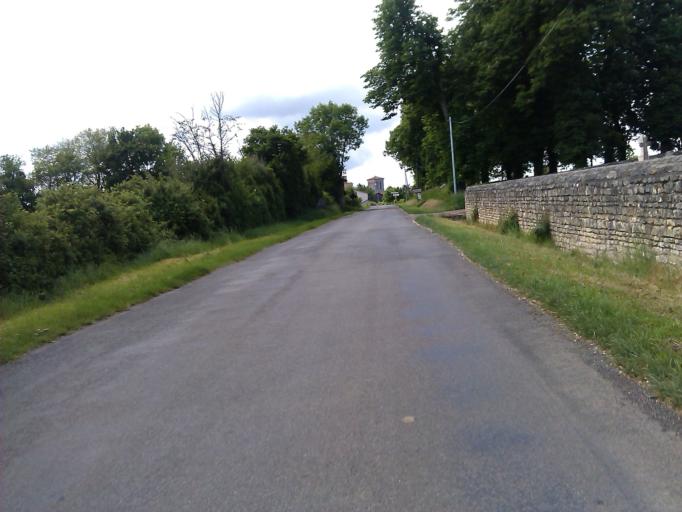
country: FR
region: Poitou-Charentes
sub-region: Departement de la Charente
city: Champagne-Mouton
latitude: 46.0413
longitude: 0.4547
